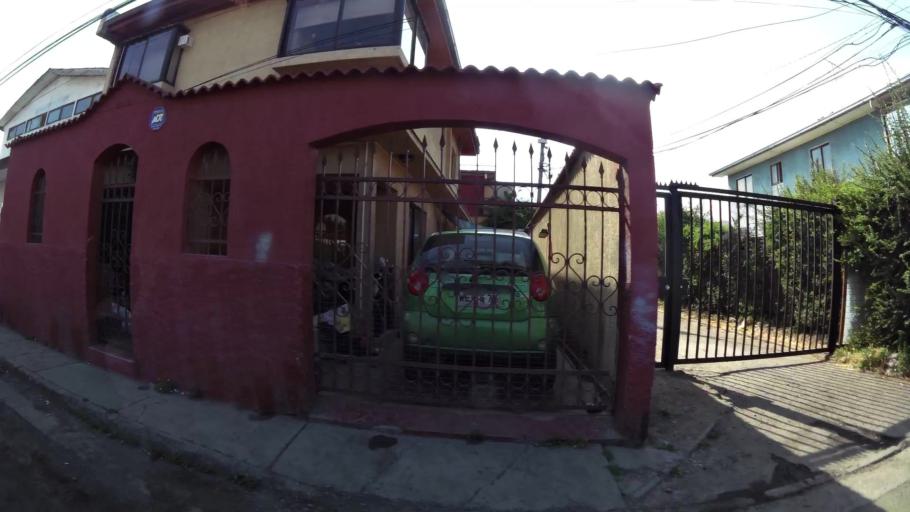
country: CL
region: Santiago Metropolitan
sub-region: Provincia de Cordillera
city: Puente Alto
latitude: -33.5619
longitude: -70.5696
